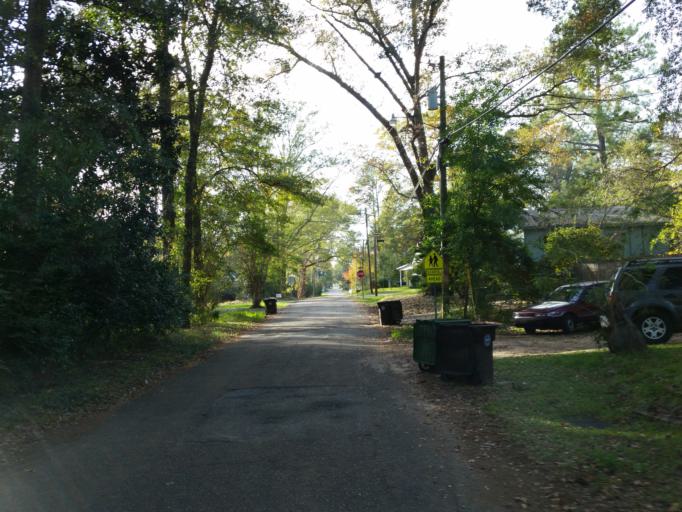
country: US
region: Mississippi
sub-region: Forrest County
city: Hattiesburg
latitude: 31.3211
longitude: -89.3198
